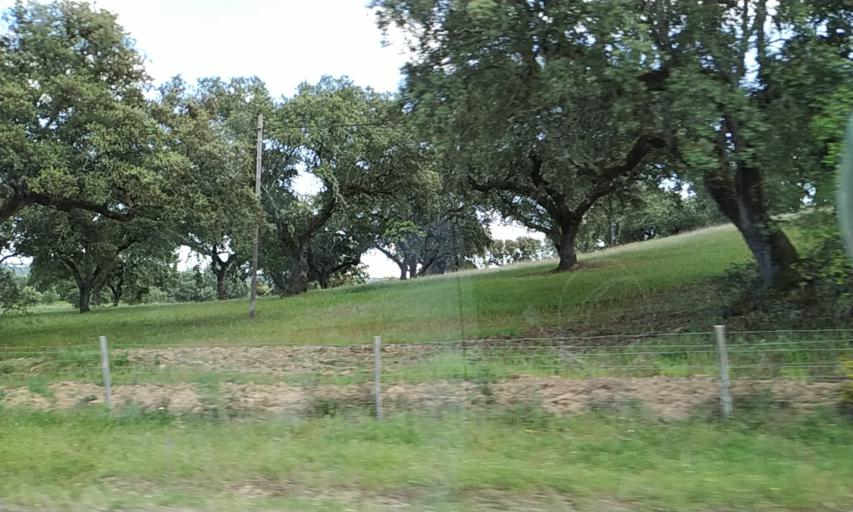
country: PT
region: Evora
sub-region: Arraiolos
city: Arraiolos
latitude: 38.7197
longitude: -8.0055
